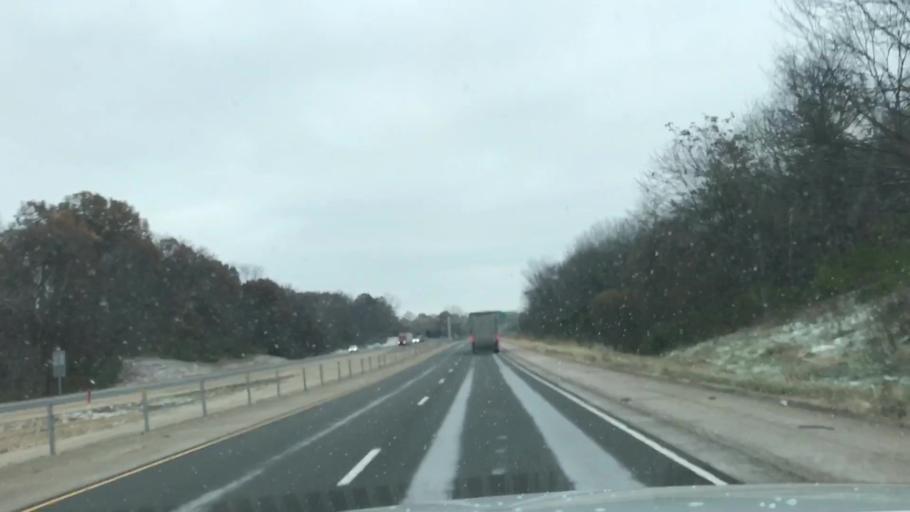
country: US
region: Illinois
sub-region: Madison County
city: Glen Carbon
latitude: 38.7568
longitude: -89.9652
